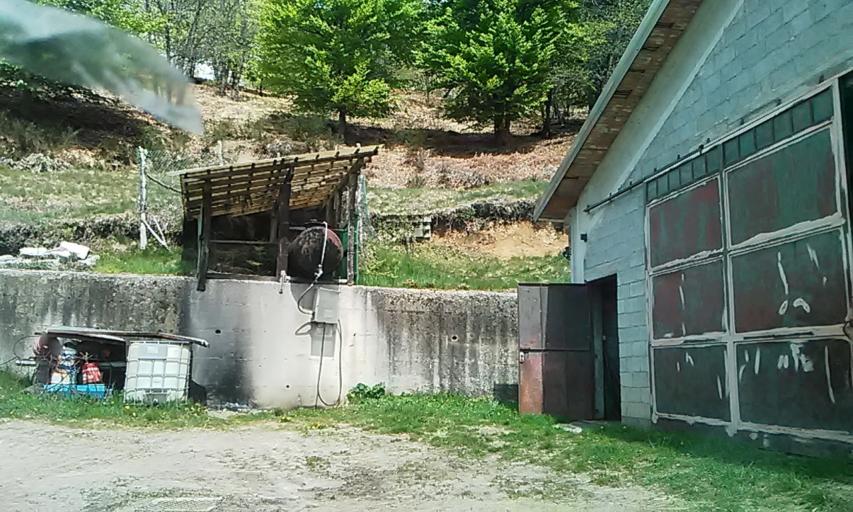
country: IT
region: Piedmont
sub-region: Provincia di Vercelli
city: Civiasco
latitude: 45.7900
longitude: 8.3047
